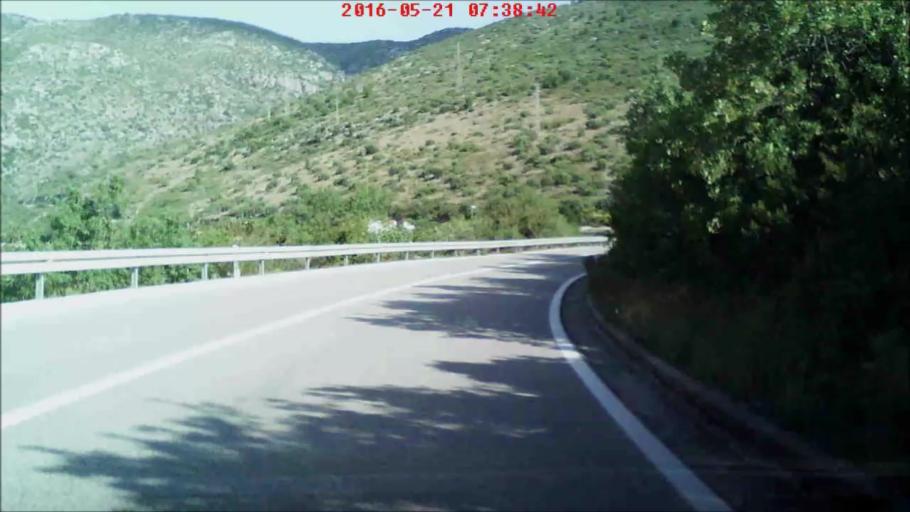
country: HR
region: Dubrovacko-Neretvanska
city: Podgora
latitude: 42.8019
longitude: 17.8480
